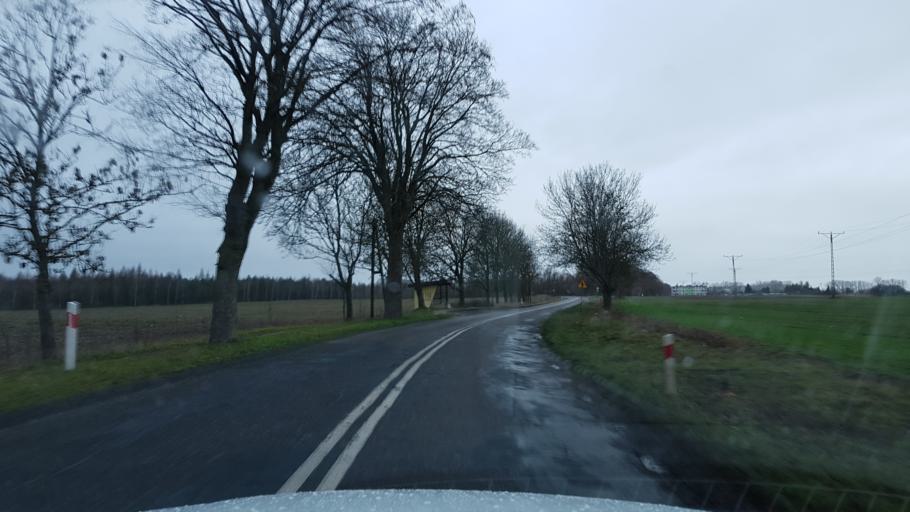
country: PL
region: West Pomeranian Voivodeship
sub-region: Powiat lobeski
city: Lobez
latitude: 53.6507
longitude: 15.5928
